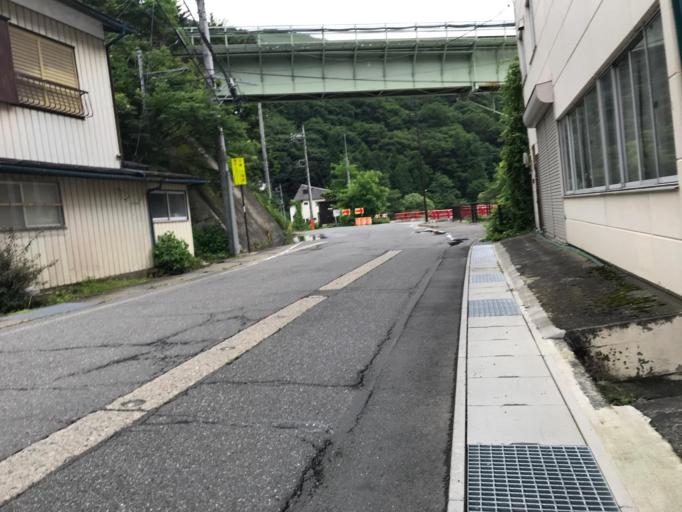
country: JP
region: Gunma
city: Numata
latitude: 36.8050
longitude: 138.9872
